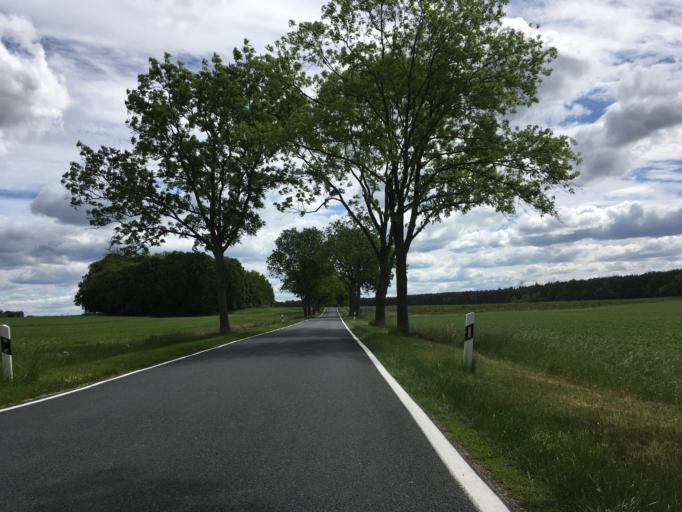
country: DE
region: Brandenburg
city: Melchow
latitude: 52.7412
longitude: 13.7254
